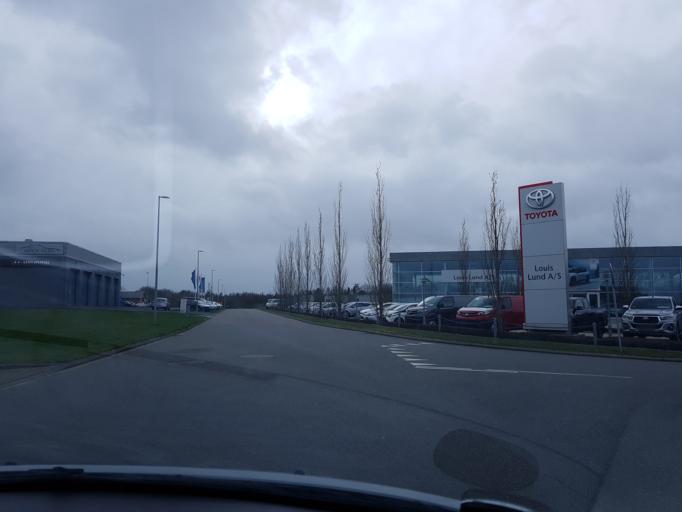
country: DK
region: South Denmark
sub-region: Varde Kommune
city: Varde
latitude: 55.6007
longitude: 8.4990
